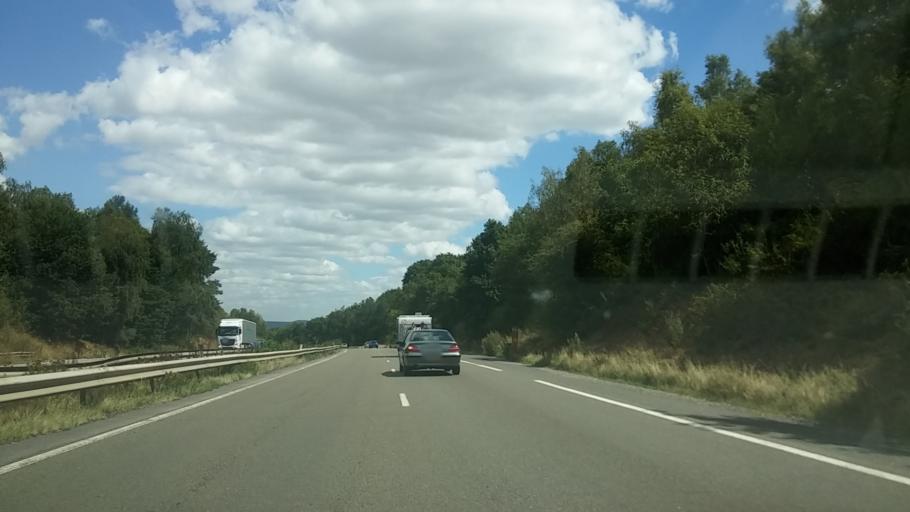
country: FR
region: Ile-de-France
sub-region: Departement des Yvelines
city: La Queue-les-Yvelines
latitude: 48.7976
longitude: 1.7563
